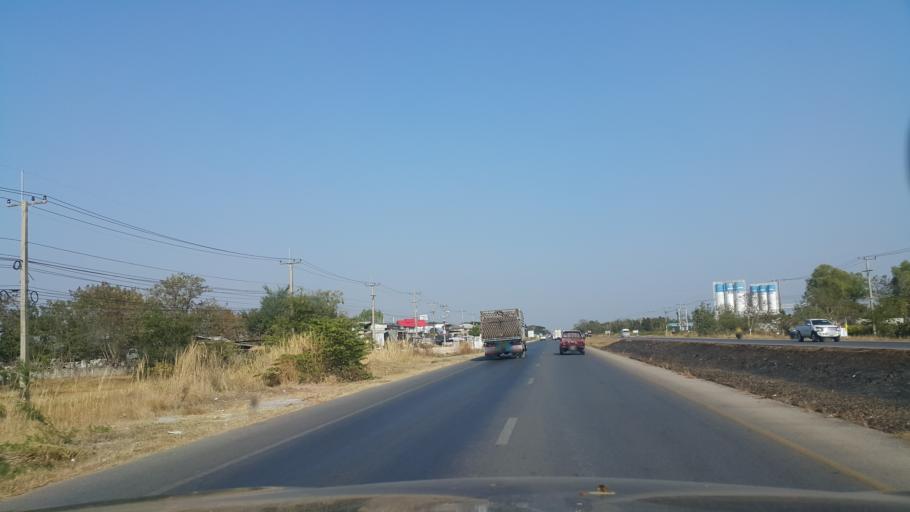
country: TH
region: Khon Kaen
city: Khon Kaen
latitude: 16.4017
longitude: 102.8740
